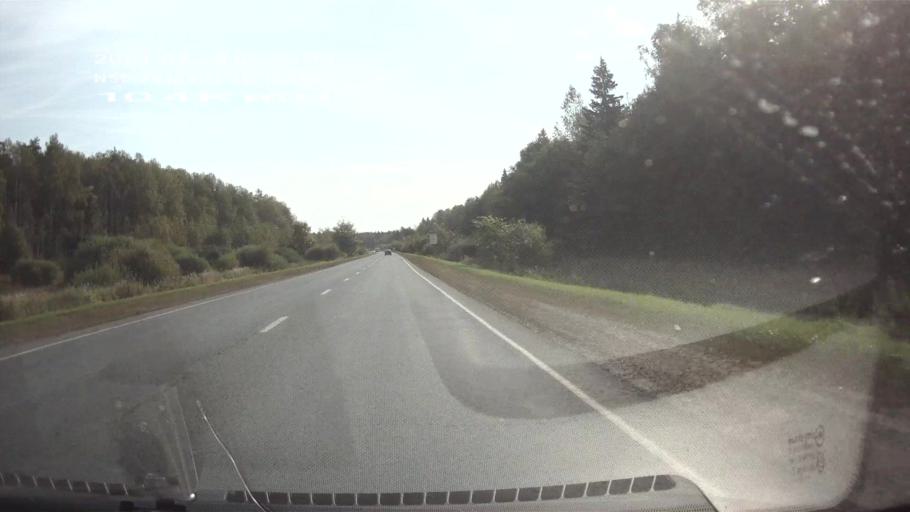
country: RU
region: Mariy-El
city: Sovetskiy
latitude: 56.7415
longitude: 48.3758
